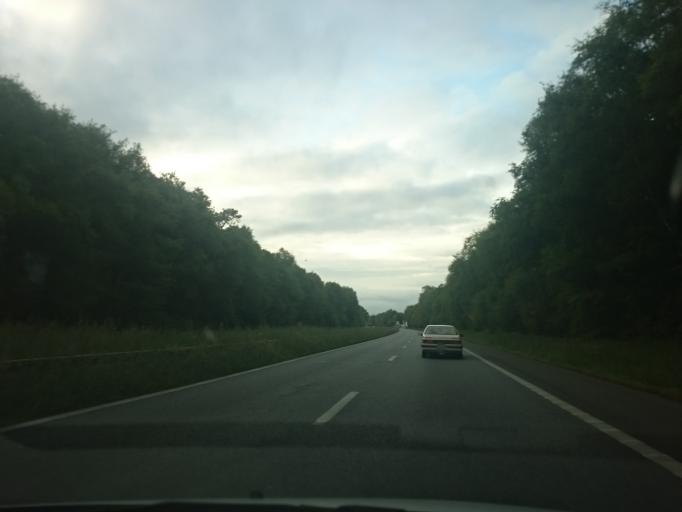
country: FR
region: Brittany
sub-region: Departement du Morbihan
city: Gestel
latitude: 47.8162
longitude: -3.4635
